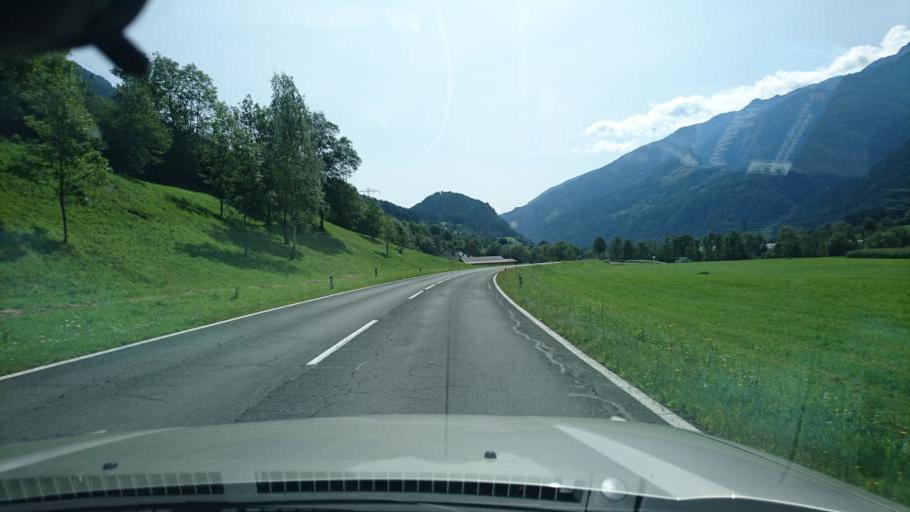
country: AT
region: Carinthia
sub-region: Politischer Bezirk Spittal an der Drau
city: Obervellach
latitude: 46.9055
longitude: 13.2560
